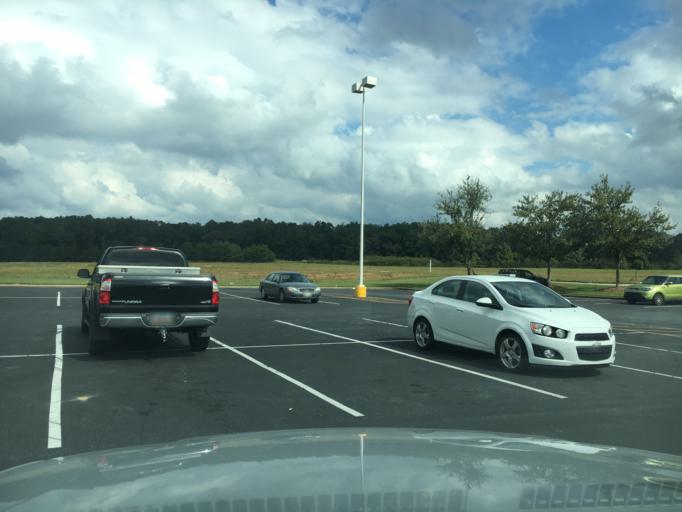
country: US
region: South Carolina
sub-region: Spartanburg County
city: Landrum
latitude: 35.1834
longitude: -82.1607
